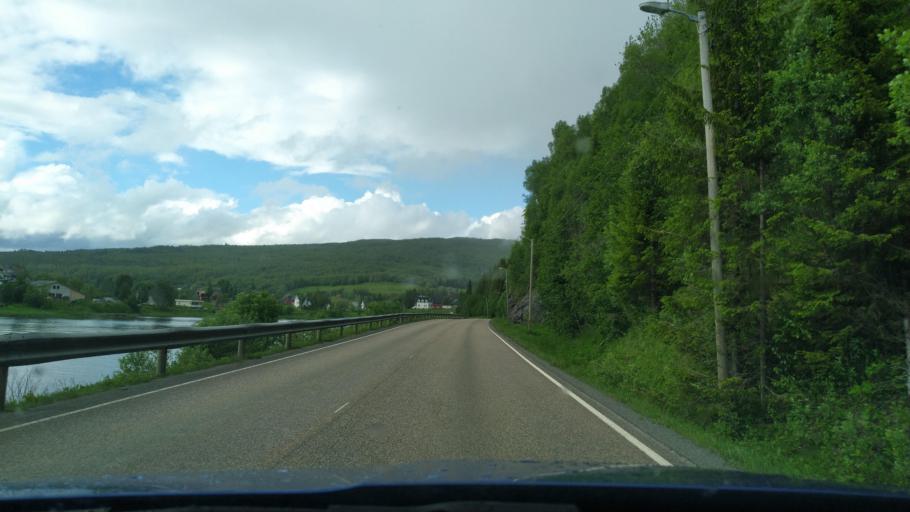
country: NO
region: Troms
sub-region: Sorreisa
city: Sorreisa
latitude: 69.1652
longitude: 18.1169
